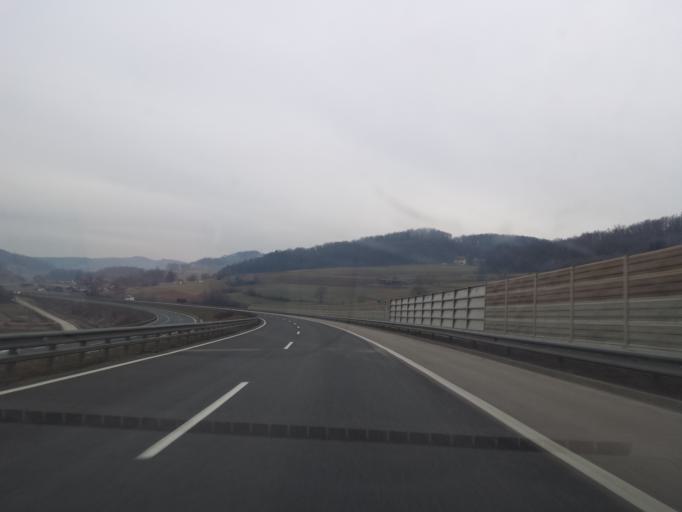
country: SI
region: Mirna Pec
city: Mirna Pec
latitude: 45.8617
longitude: 15.1399
